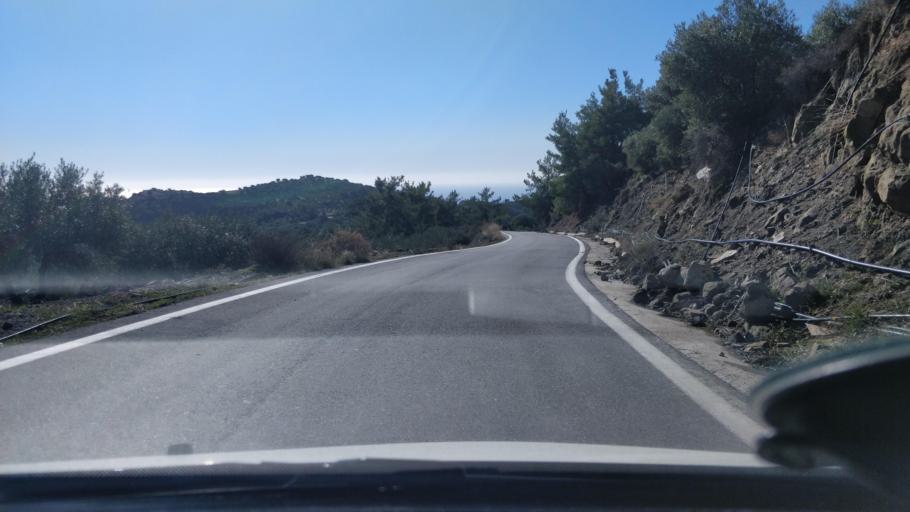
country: GR
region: Crete
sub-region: Nomos Irakleiou
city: Kastelli
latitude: 35.0242
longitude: 25.4486
